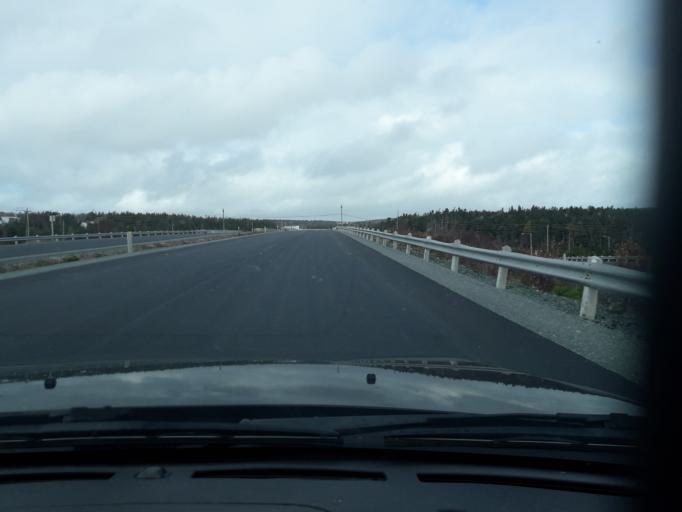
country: CA
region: Newfoundland and Labrador
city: Mount Pearl
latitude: 47.5605
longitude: -52.7788
